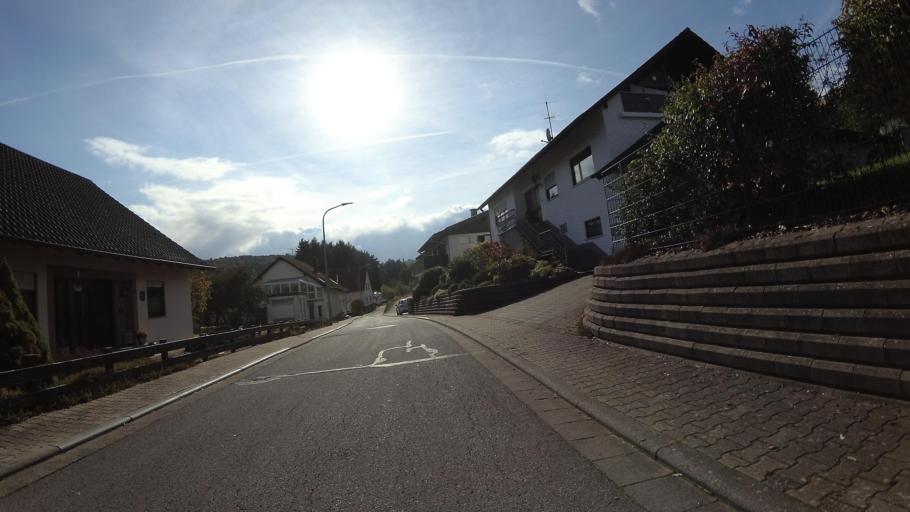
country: DE
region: Rheinland-Pfalz
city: Ohmbach
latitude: 49.4468
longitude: 7.3485
